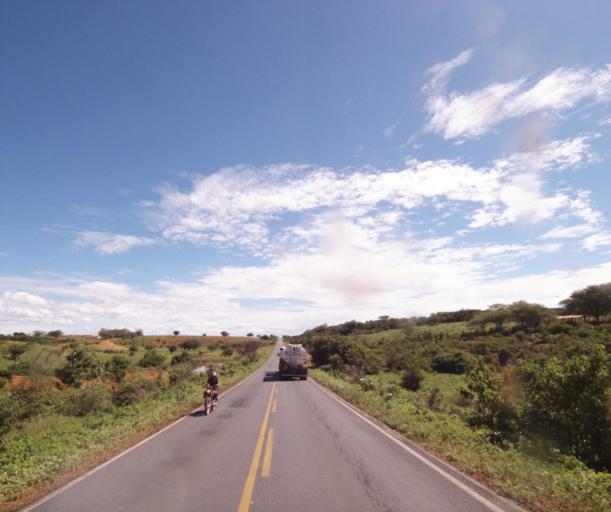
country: BR
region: Bahia
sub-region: Guanambi
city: Guanambi
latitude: -14.5251
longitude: -42.6958
